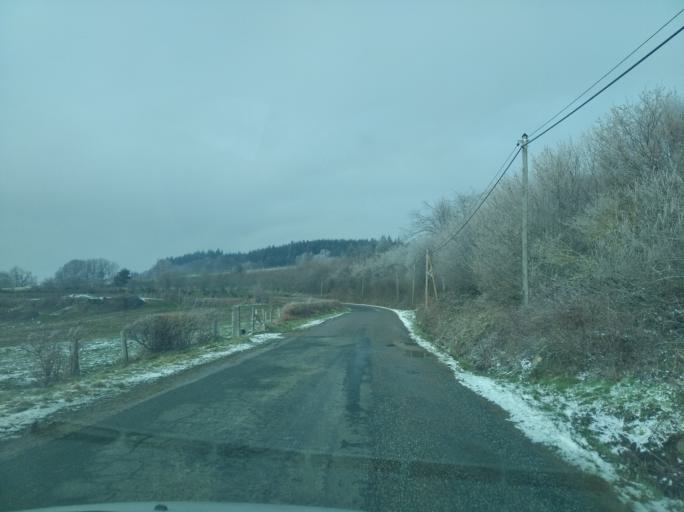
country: FR
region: Rhone-Alpes
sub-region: Departement de la Loire
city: Ambierle
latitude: 46.1120
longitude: 3.8061
